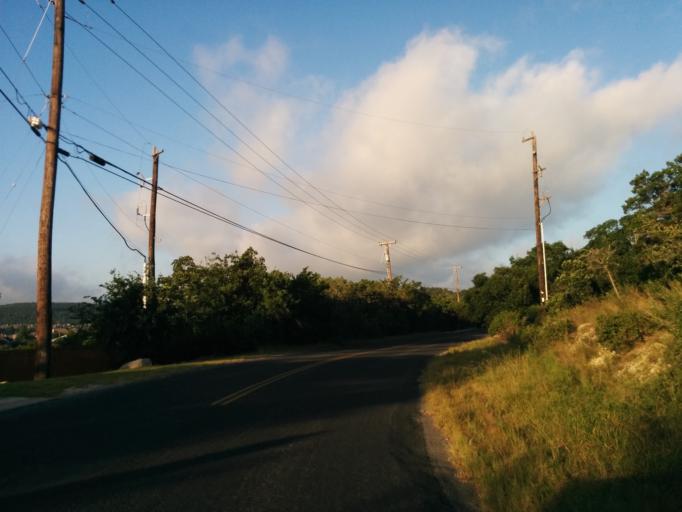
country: US
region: Texas
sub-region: Bexar County
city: Cross Mountain
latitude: 29.6560
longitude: -98.6348
